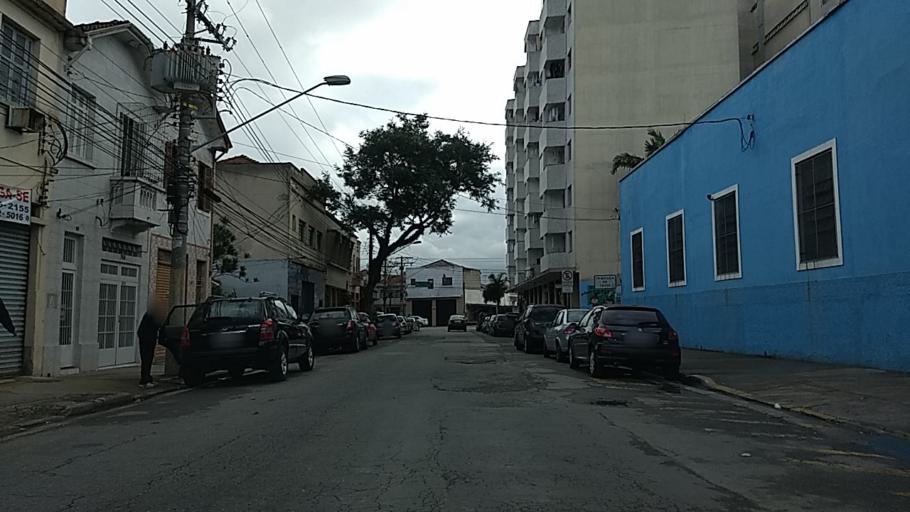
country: BR
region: Sao Paulo
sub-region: Sao Paulo
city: Sao Paulo
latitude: -23.5409
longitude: -46.5968
